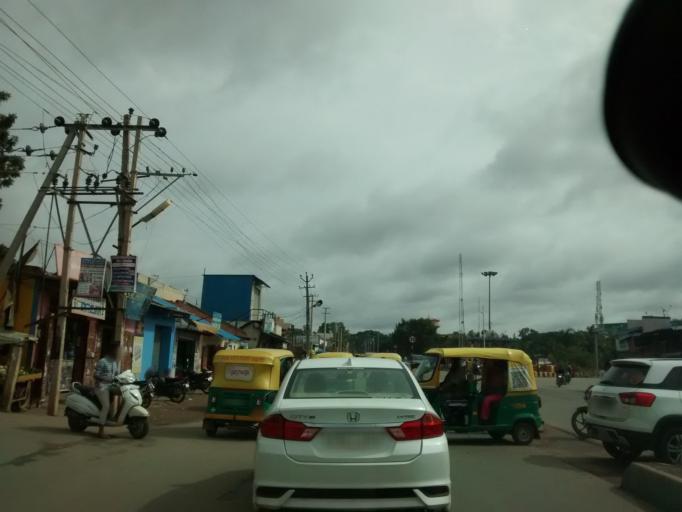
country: IN
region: Karnataka
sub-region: Tumkur
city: Tumkur
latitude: 13.3617
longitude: 77.1033
